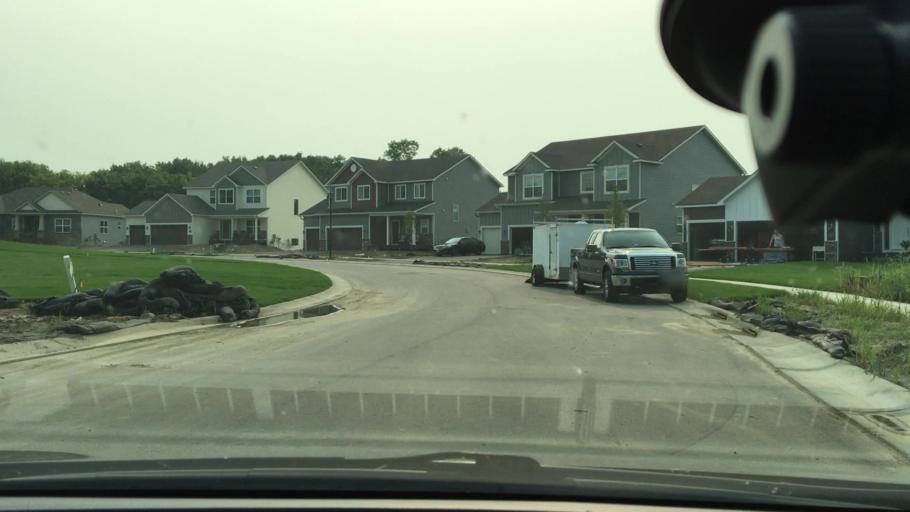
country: US
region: Minnesota
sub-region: Hennepin County
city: Champlin
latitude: 45.1934
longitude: -93.4456
